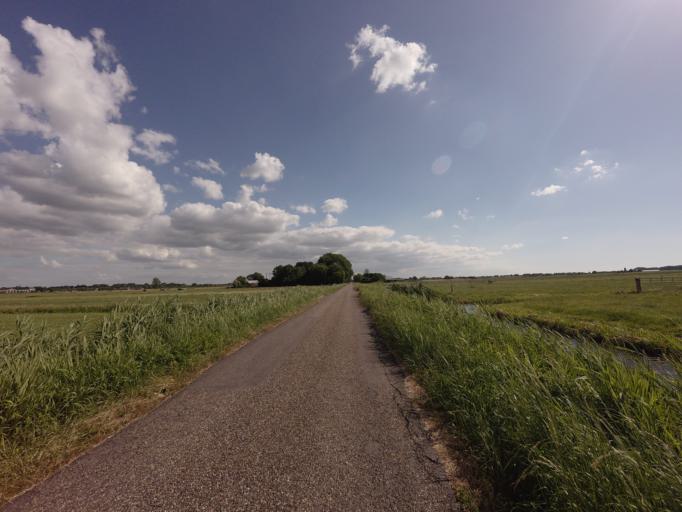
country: NL
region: Utrecht
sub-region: Gemeente De Ronde Venen
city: Mijdrecht
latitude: 52.2226
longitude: 4.8495
